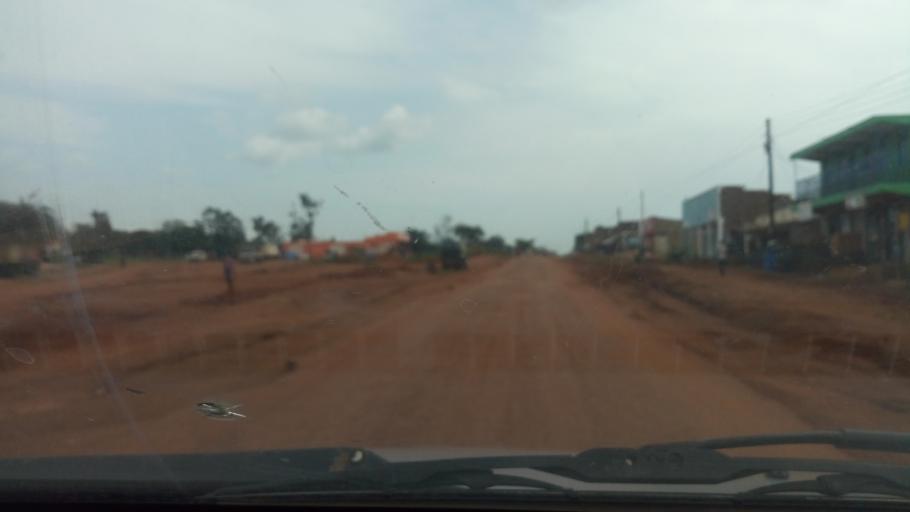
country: UG
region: Western Region
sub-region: Kiryandongo District
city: Kiryandongo
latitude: 1.8099
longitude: 32.0088
